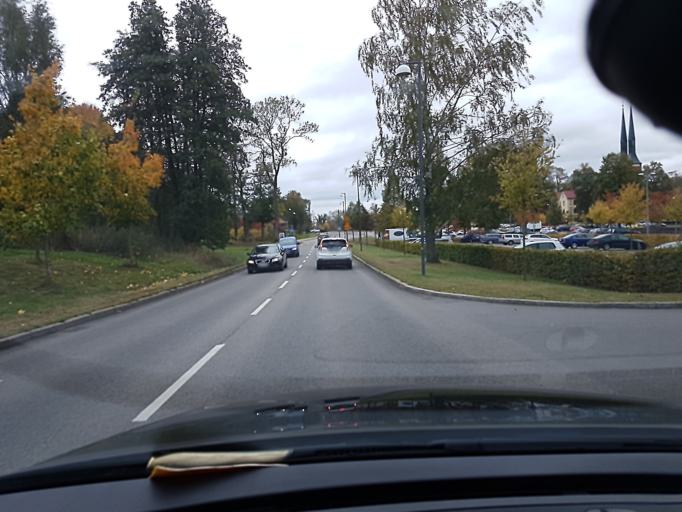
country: SE
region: Kronoberg
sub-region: Vaxjo Kommun
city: Vaexjoe
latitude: 56.8800
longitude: 14.8152
